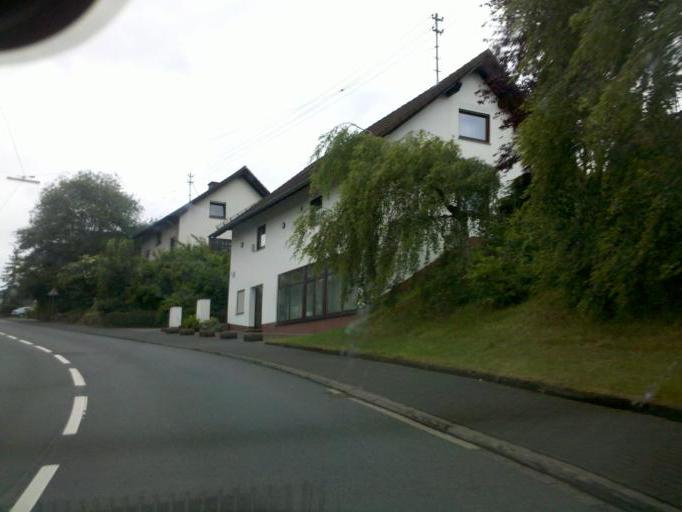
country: DE
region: North Rhine-Westphalia
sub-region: Regierungsbezirk Arnsberg
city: Wilnsdorf
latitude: 50.8140
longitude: 8.1039
